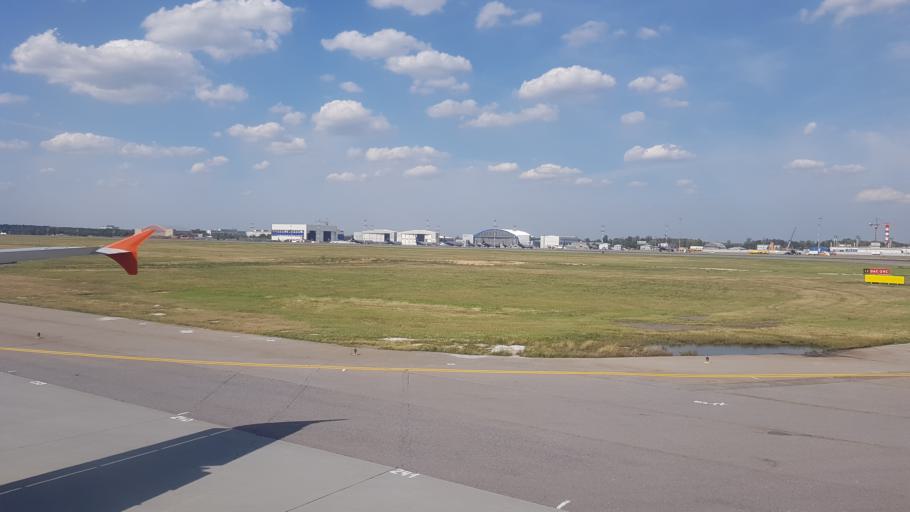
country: RU
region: Moskovskaya
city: Novopodrezkovo
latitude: 55.9714
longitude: 37.4132
